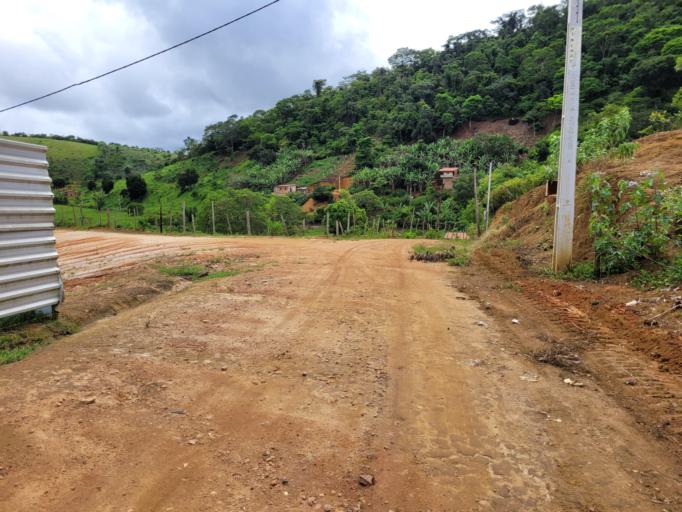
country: BR
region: Bahia
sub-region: Mutuipe
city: Mutuipe
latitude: -13.2581
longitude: -39.5635
